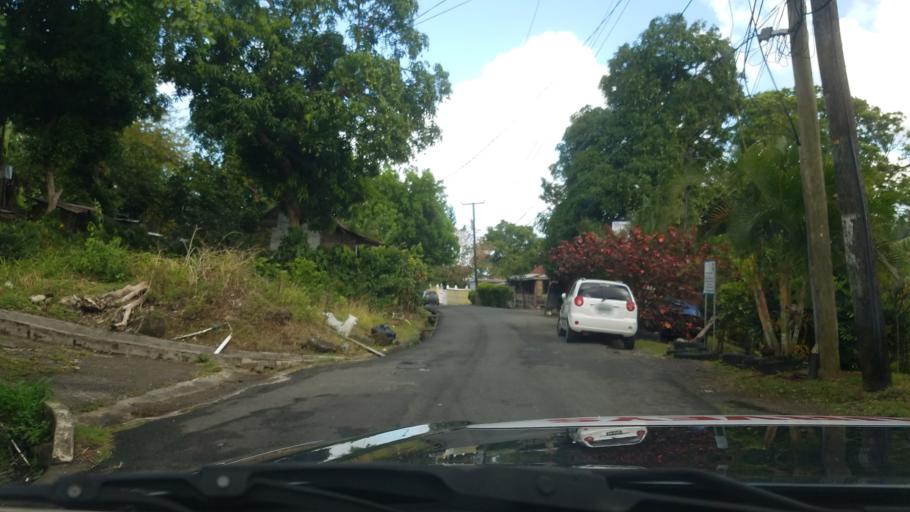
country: LC
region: Castries Quarter
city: Bisee
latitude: 14.0244
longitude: -60.9773
